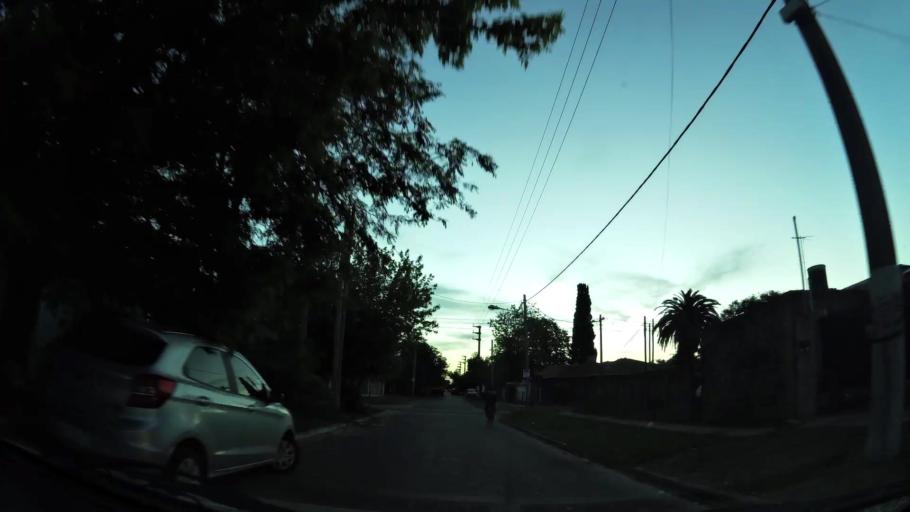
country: AR
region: Buenos Aires
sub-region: Partido de Quilmes
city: Quilmes
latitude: -34.7714
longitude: -58.2037
